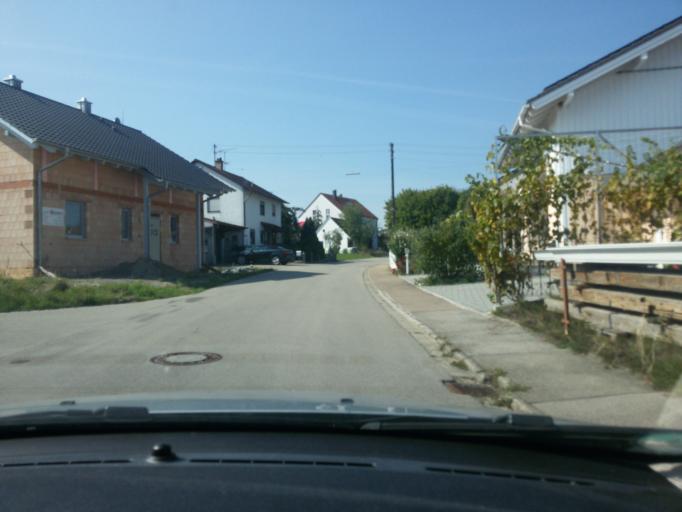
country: DE
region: Bavaria
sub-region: Swabia
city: Scherstetten
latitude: 48.1798
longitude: 10.6380
